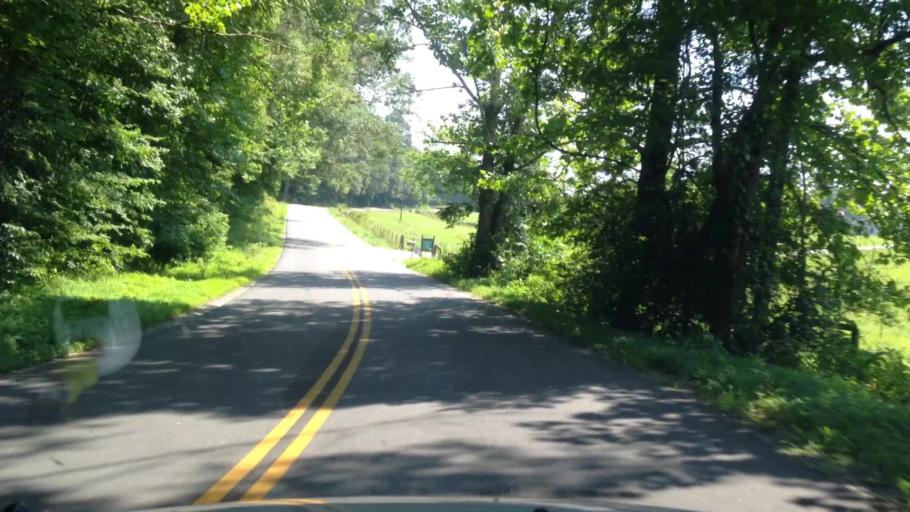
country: US
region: Virginia
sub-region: Patrick County
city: Patrick Springs
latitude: 36.5741
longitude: -80.1963
